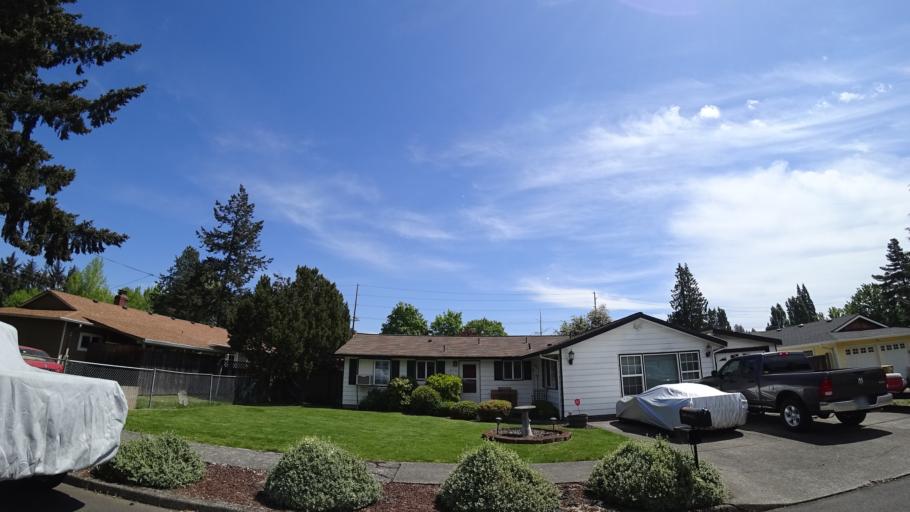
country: US
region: Oregon
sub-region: Washington County
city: Aloha
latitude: 45.4903
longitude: -122.8532
